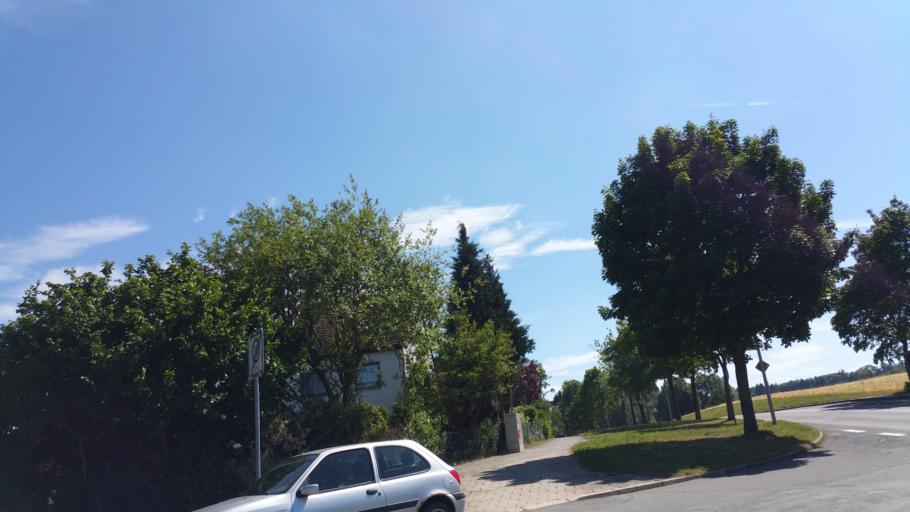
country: DE
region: Bavaria
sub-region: Upper Franconia
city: Hof
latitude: 50.3339
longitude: 11.8942
